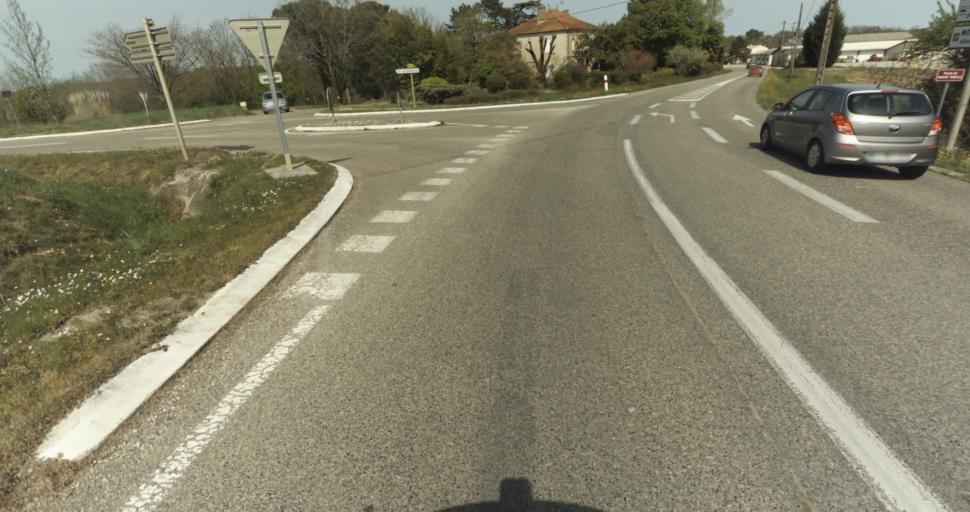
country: FR
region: Midi-Pyrenees
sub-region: Departement du Tarn-et-Garonne
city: Moissac
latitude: 44.1681
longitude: 1.0871
